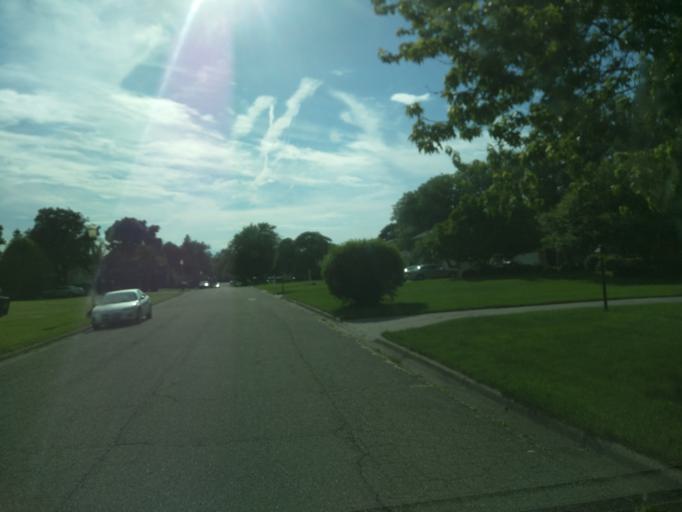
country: US
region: Michigan
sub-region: Ingham County
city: Edgemont Park
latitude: 42.7494
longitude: -84.6077
